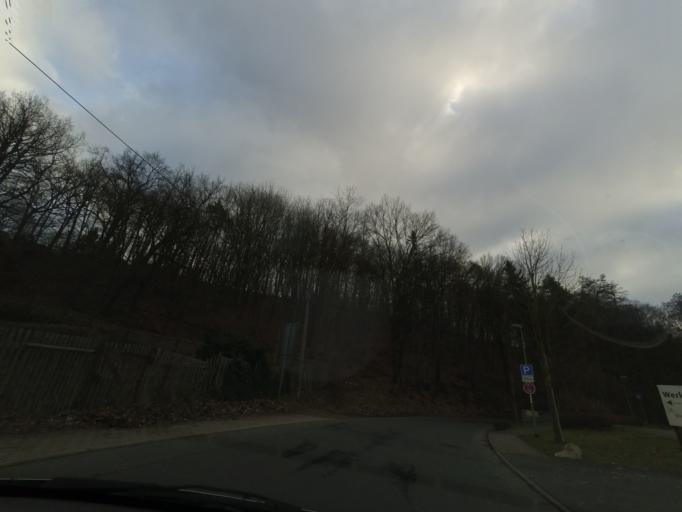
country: DE
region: Thuringia
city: Saalfeld
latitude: 50.6377
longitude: 11.3453
